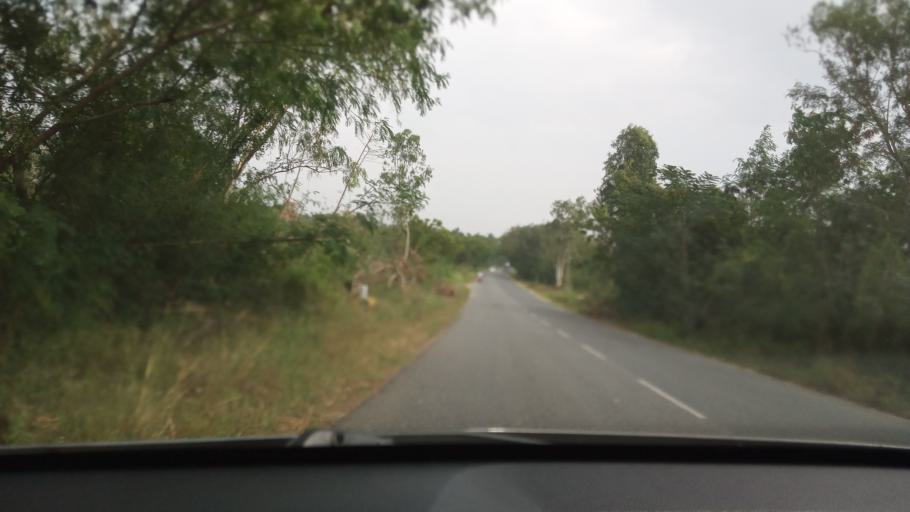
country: IN
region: Andhra Pradesh
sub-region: Chittoor
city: Pakala
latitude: 13.6561
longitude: 78.8516
